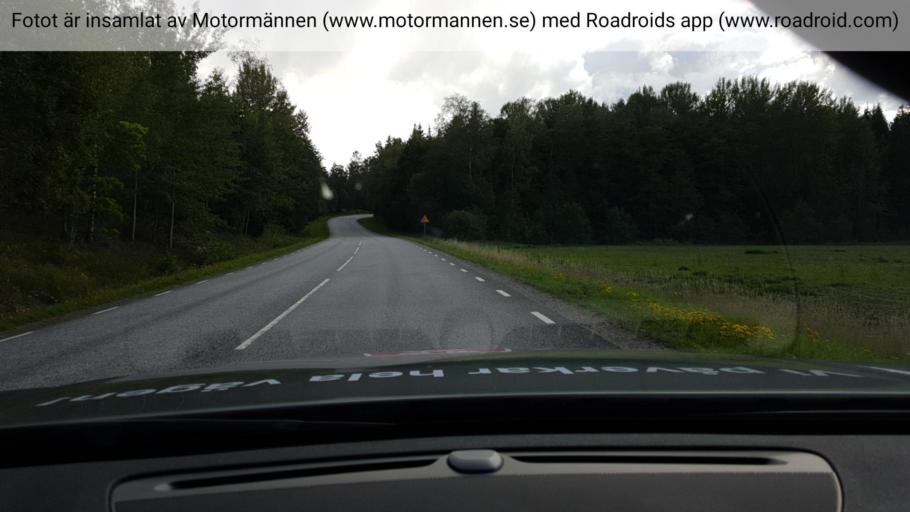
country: SE
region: Soedermanland
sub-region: Strangnas Kommun
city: Stallarholmen
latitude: 59.3409
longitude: 17.1168
